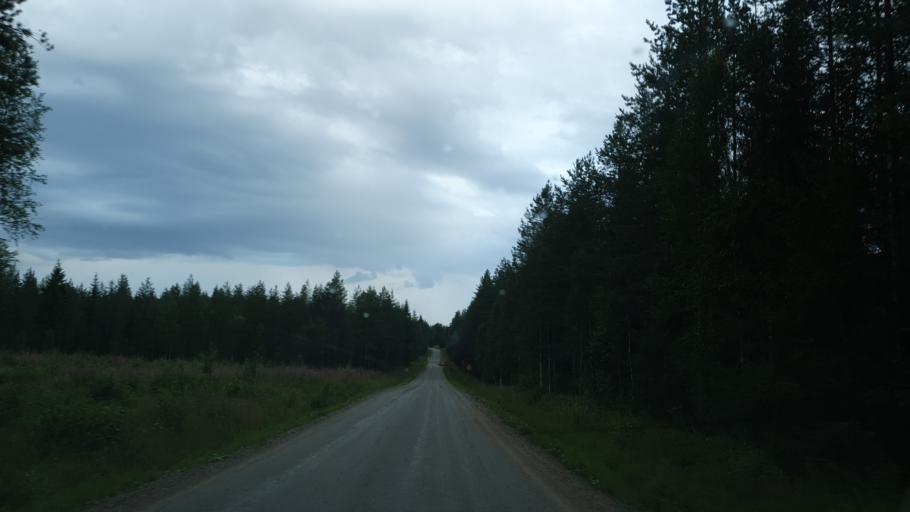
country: FI
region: Kainuu
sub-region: Kehys-Kainuu
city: Kuhmo
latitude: 64.2108
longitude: 29.3698
